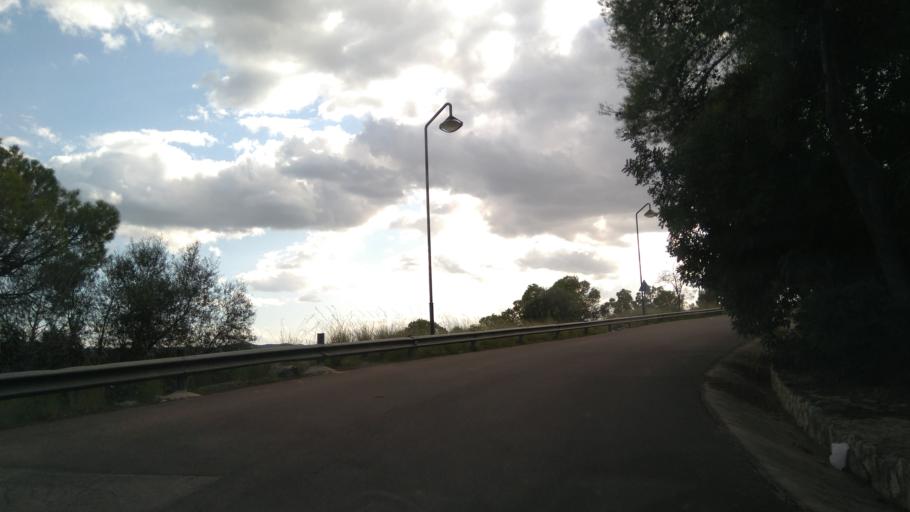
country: ES
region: Valencia
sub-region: Provincia de Valencia
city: Alzira
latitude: 39.1530
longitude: -0.4173
